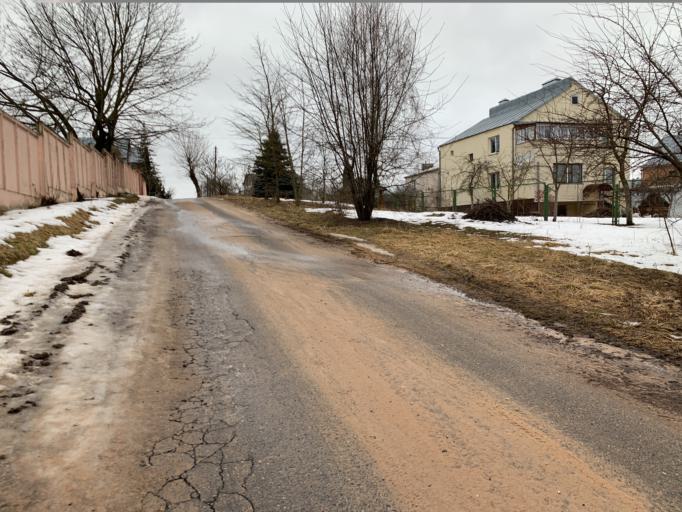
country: BY
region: Minsk
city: Nyasvizh
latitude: 53.2299
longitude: 26.6807
